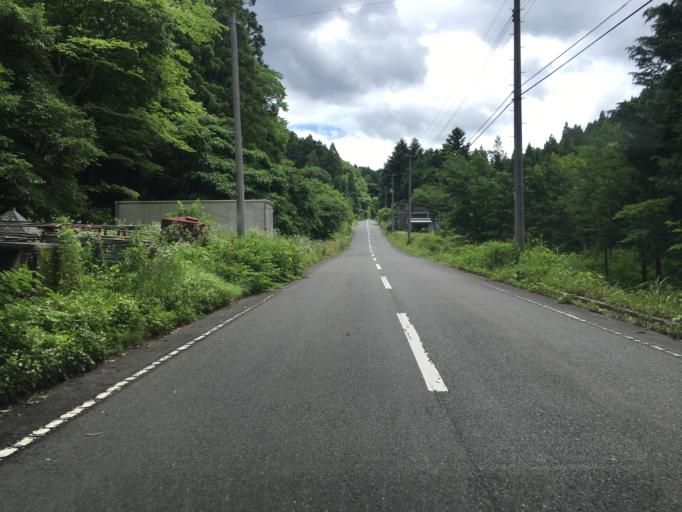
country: JP
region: Miyagi
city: Marumori
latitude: 37.7173
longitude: 140.8853
